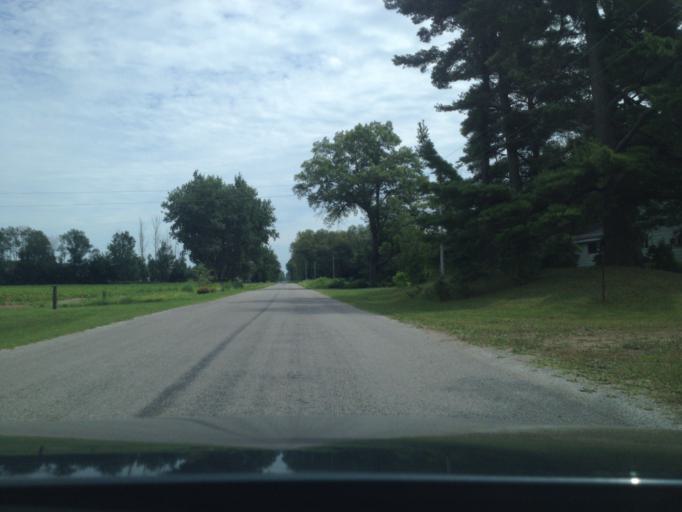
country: CA
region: Ontario
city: Norfolk County
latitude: 42.8520
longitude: -80.4200
